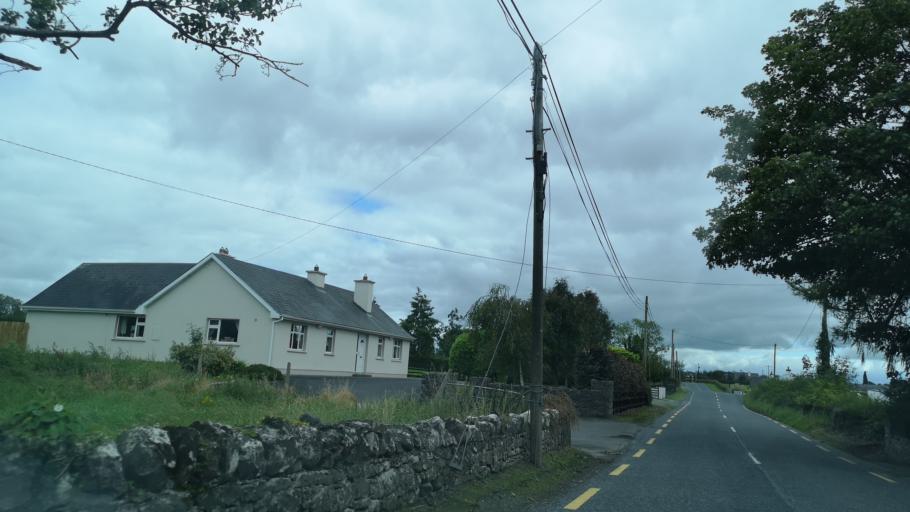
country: IE
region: Connaught
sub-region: County Galway
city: Ballinasloe
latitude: 53.3021
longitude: -8.1312
